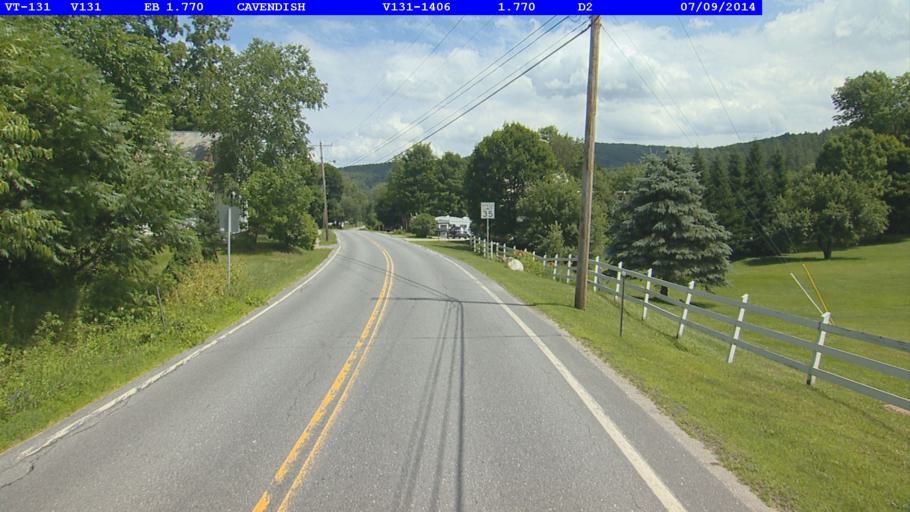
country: US
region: Vermont
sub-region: Windsor County
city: Chester
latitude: 43.3830
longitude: -72.6144
